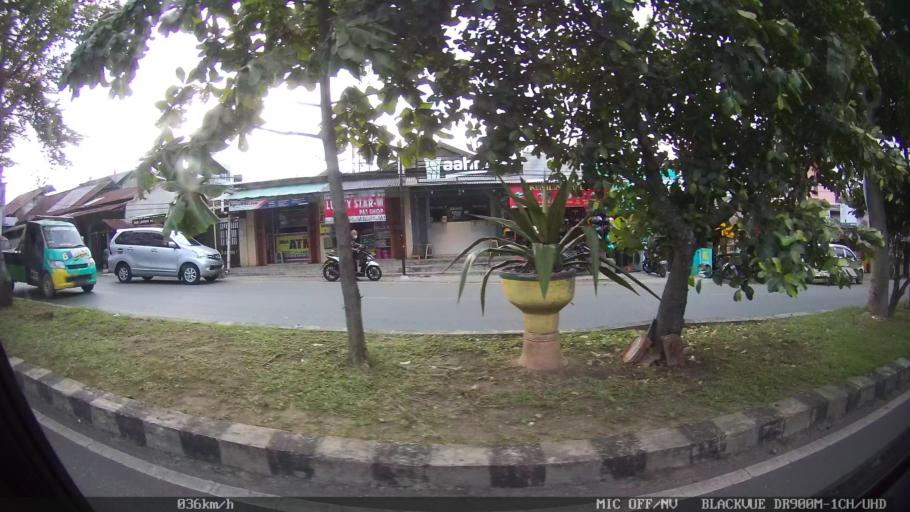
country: ID
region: Lampung
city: Kedaton
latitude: -5.3956
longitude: 105.2139
